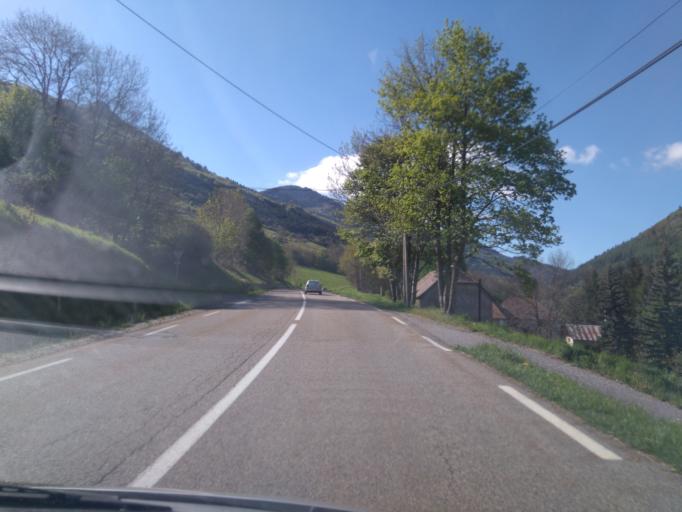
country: FR
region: Rhone-Alpes
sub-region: Departement de l'Isere
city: Mens
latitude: 44.6920
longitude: 5.6861
